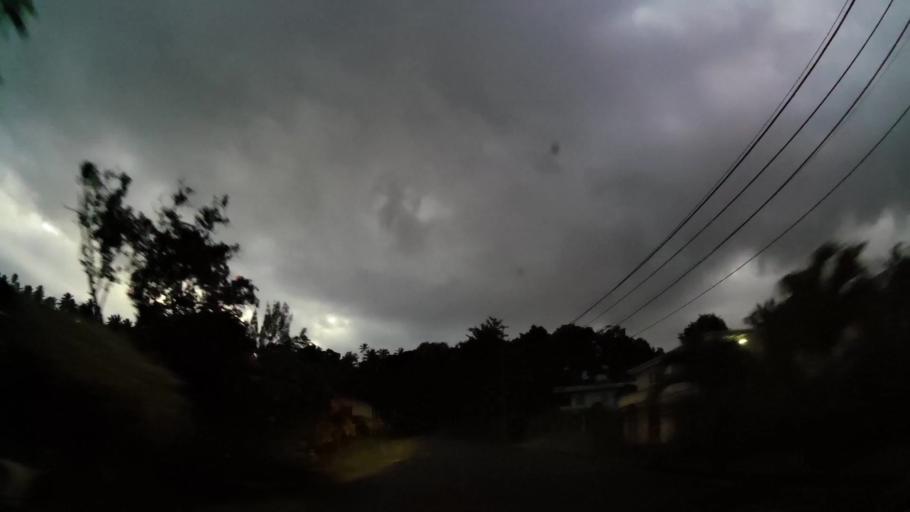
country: DM
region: Saint Andrew
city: Calibishie
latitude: 15.5907
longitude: -61.3400
